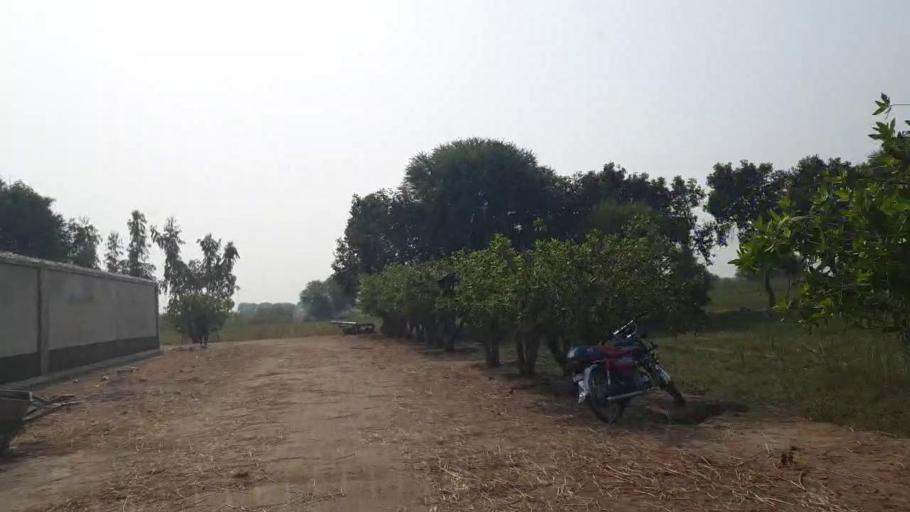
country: PK
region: Sindh
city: Matli
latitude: 25.1263
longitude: 68.6905
